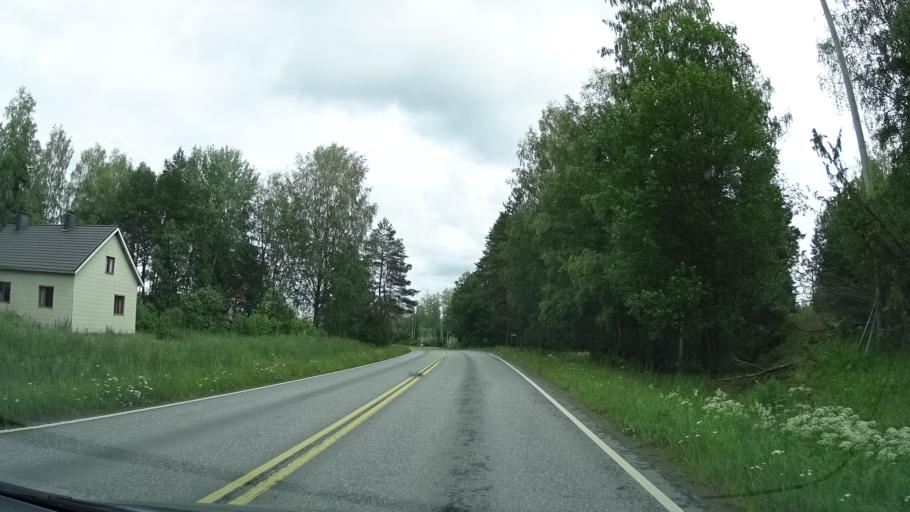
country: FI
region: Pirkanmaa
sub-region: Etelae-Pirkanmaa
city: Urjala
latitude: 61.0879
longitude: 23.4789
